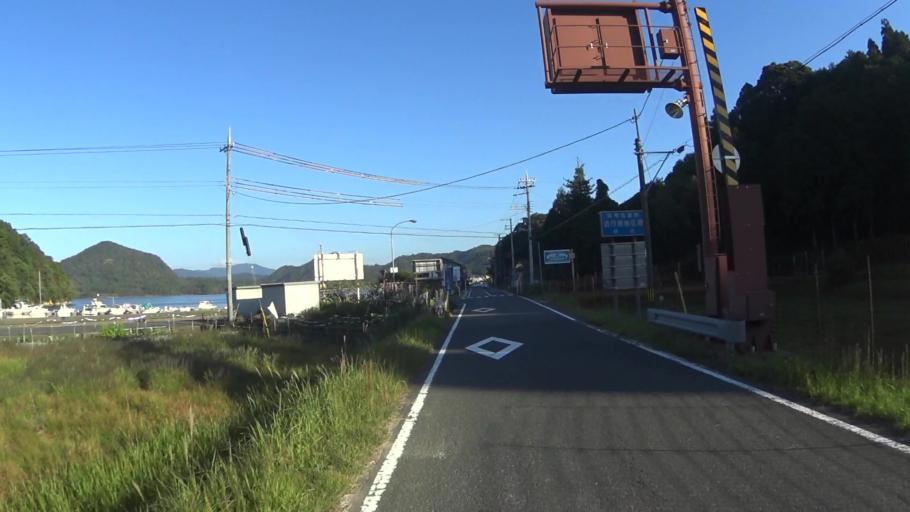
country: JP
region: Hyogo
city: Toyooka
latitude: 35.6112
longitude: 134.8876
